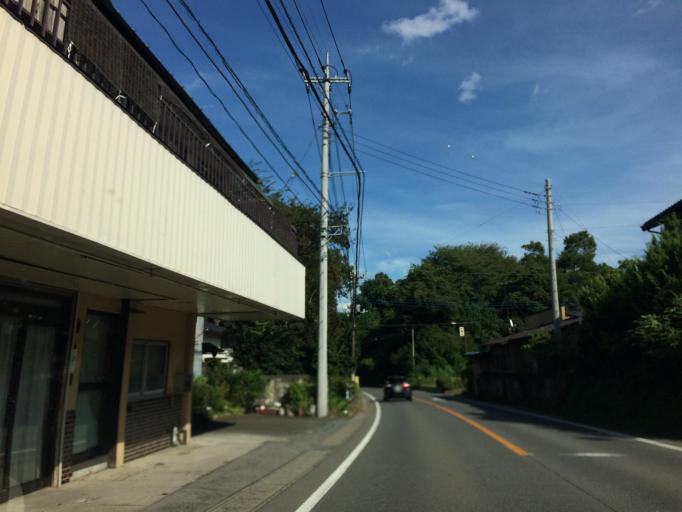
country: JP
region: Gunma
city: Nakanojomachi
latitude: 36.5656
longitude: 138.8794
